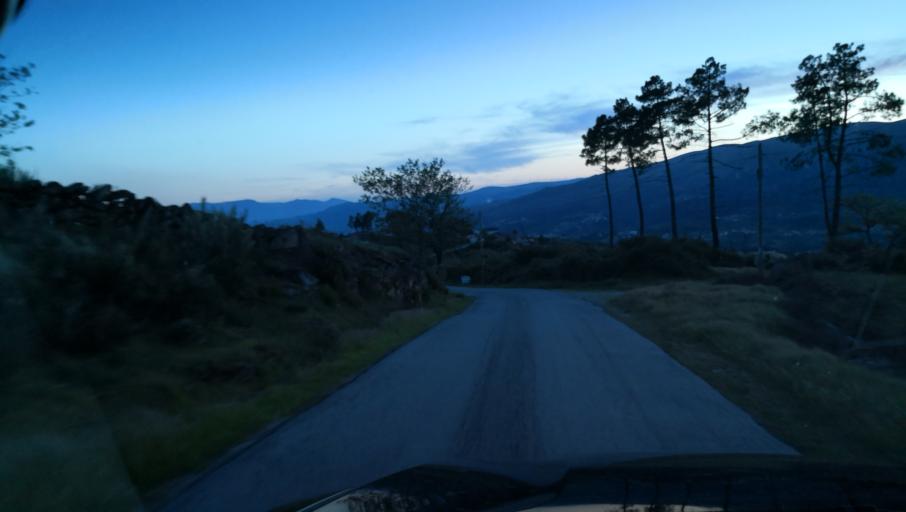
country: PT
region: Vila Real
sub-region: Vila Real
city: Vila Real
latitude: 41.3518
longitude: -7.6791
